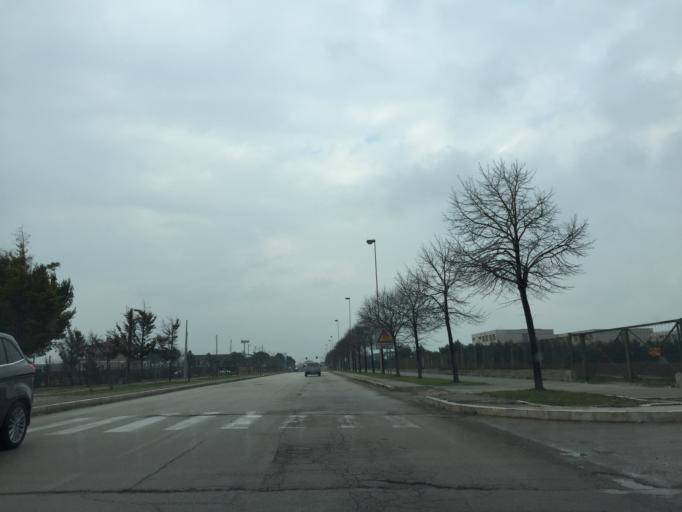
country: IT
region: Apulia
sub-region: Provincia di Foggia
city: Foggia
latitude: 41.4540
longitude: 15.5237
